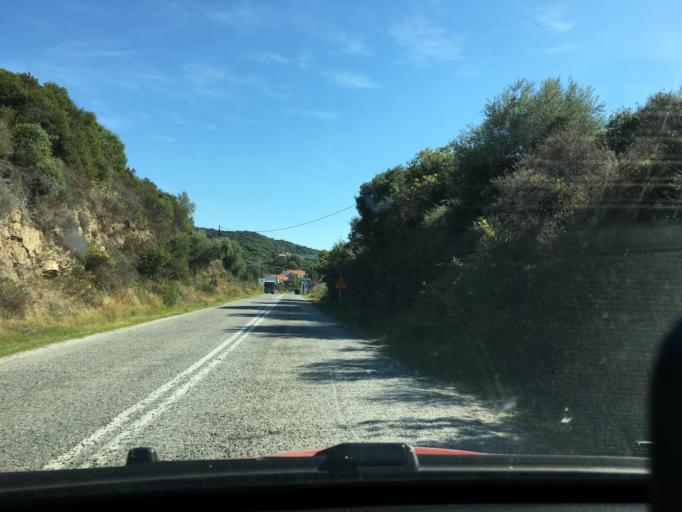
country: GR
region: Central Macedonia
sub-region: Nomos Chalkidikis
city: Ouranoupolis
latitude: 40.3496
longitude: 23.9587
